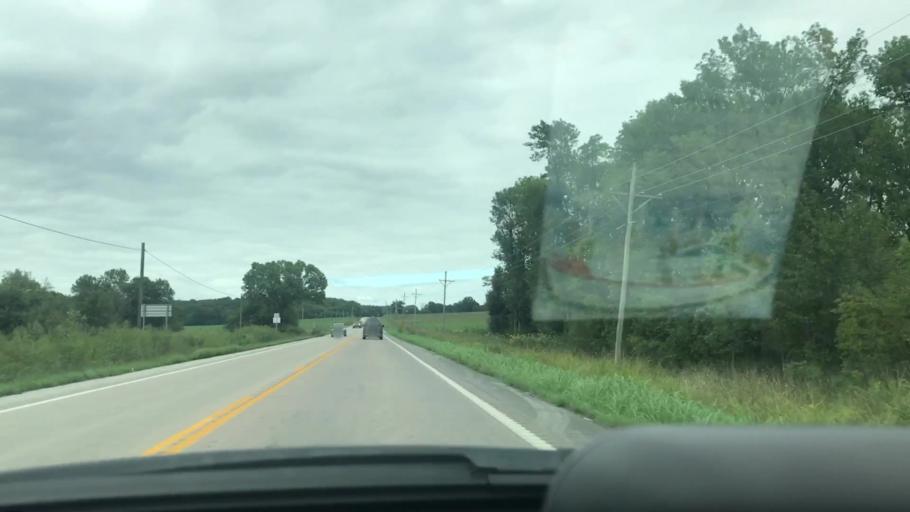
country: US
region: Missouri
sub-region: Hickory County
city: Hermitage
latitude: 37.8622
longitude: -93.1779
